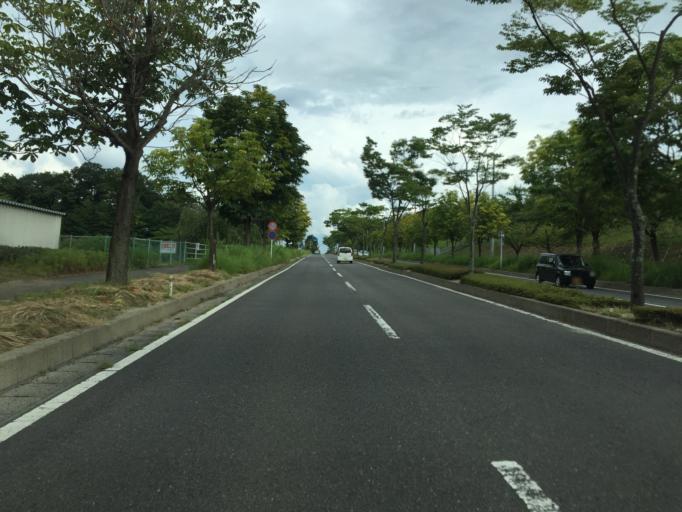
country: JP
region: Fukushima
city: Fukushima-shi
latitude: 37.6911
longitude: 140.4733
